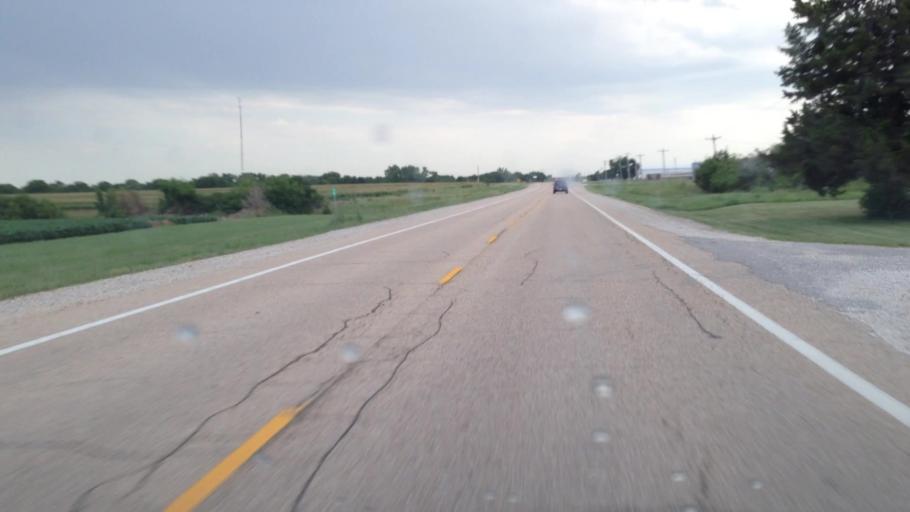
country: US
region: Kansas
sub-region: Coffey County
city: Burlington
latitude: 38.1740
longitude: -95.7389
